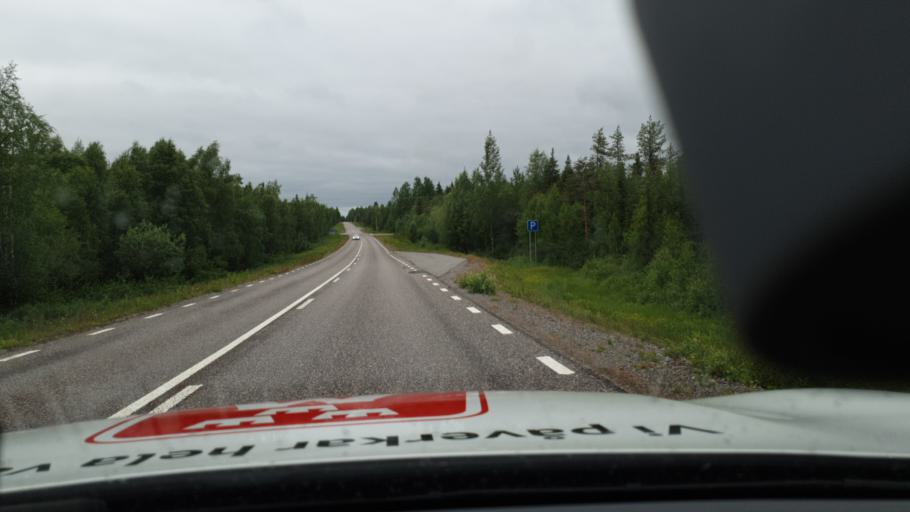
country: SE
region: Norrbotten
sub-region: Pajala Kommun
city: Pajala
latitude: 67.1863
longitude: 23.4838
